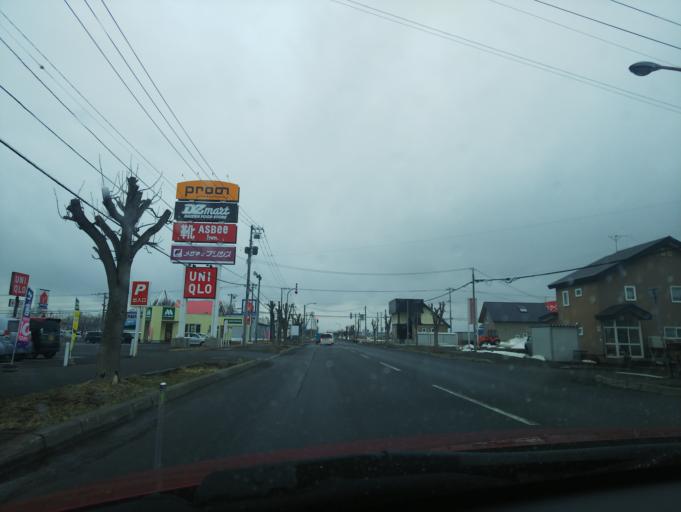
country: JP
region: Hokkaido
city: Nayoro
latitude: 44.3372
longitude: 142.4503
